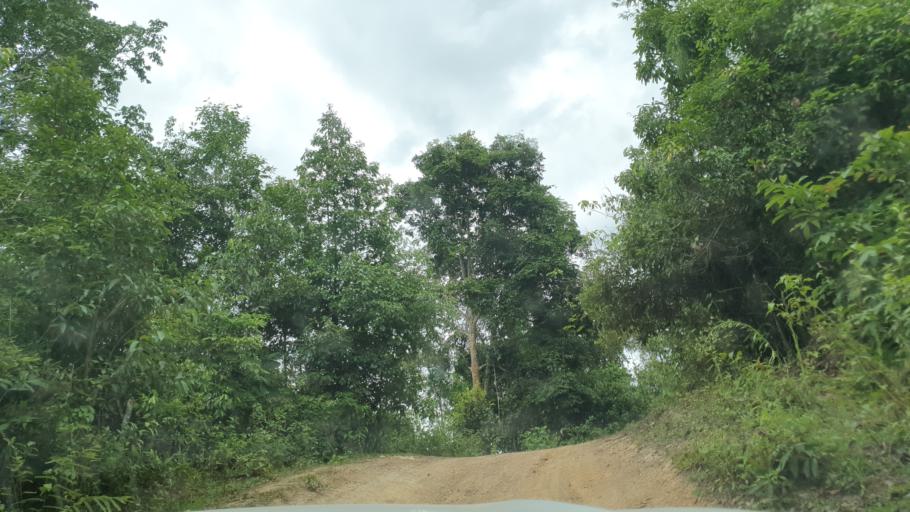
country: VN
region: Nghe An
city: Muong Xen
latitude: 19.3272
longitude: 103.7318
